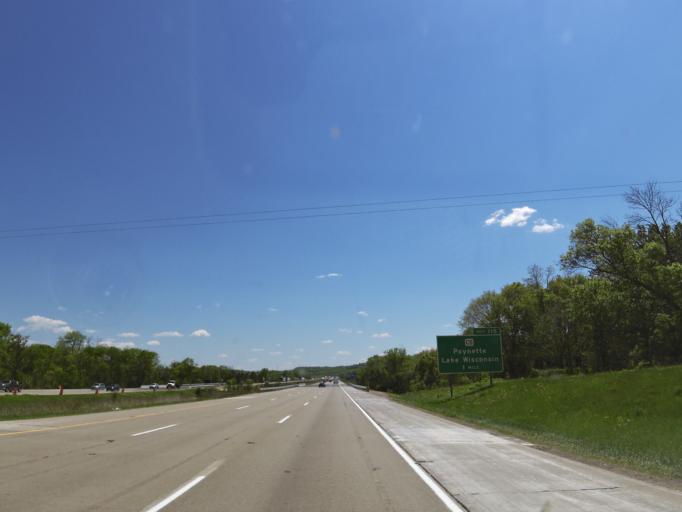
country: US
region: Wisconsin
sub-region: Columbia County
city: Poynette
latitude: 43.4071
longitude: -89.4672
